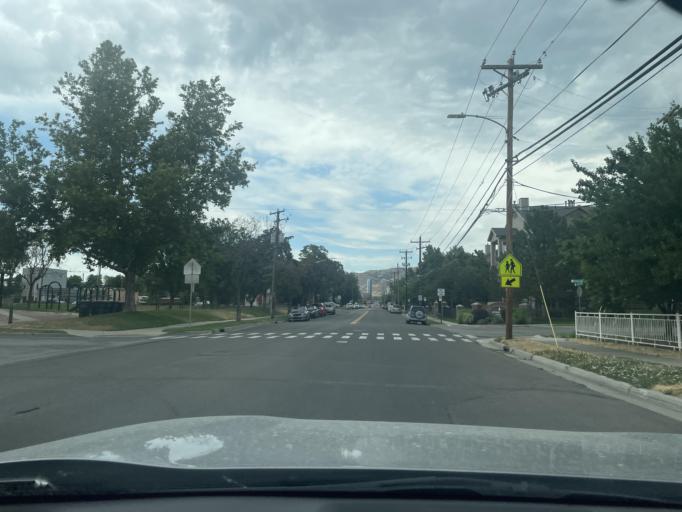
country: US
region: Utah
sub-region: Salt Lake County
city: Salt Lake City
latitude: 40.7445
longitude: -111.8939
